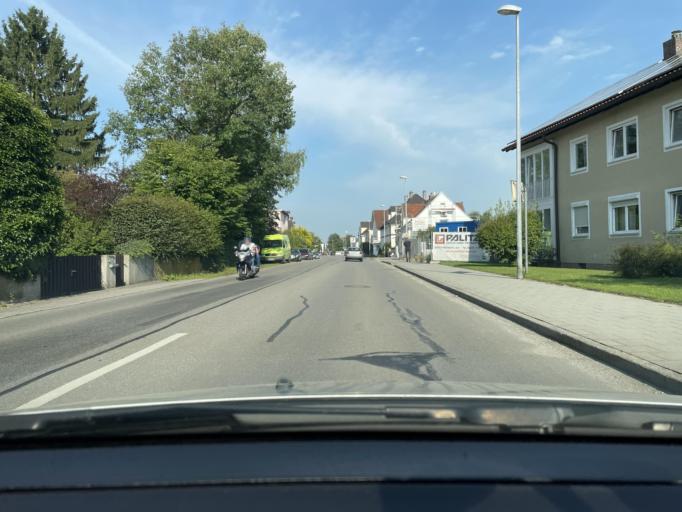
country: DE
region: Bavaria
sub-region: Upper Bavaria
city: Muehldorf
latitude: 48.2449
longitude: 12.5129
